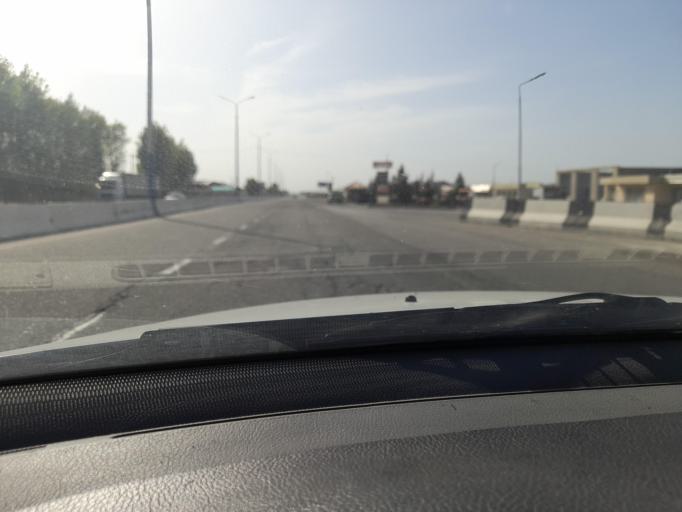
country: UZ
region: Samarqand
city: Kattaqo'rg'on
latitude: 39.9180
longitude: 66.3025
